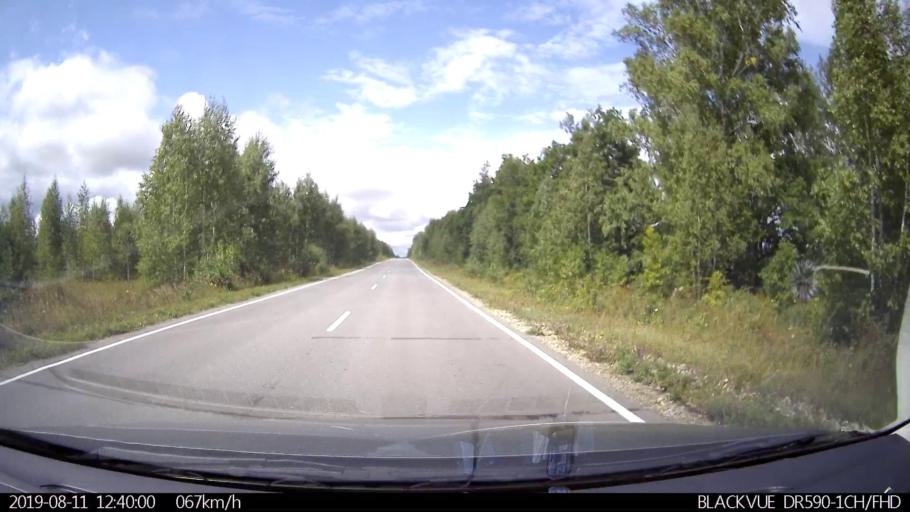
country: RU
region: Ulyanovsk
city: Ignatovka
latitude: 53.8362
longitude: 47.7875
